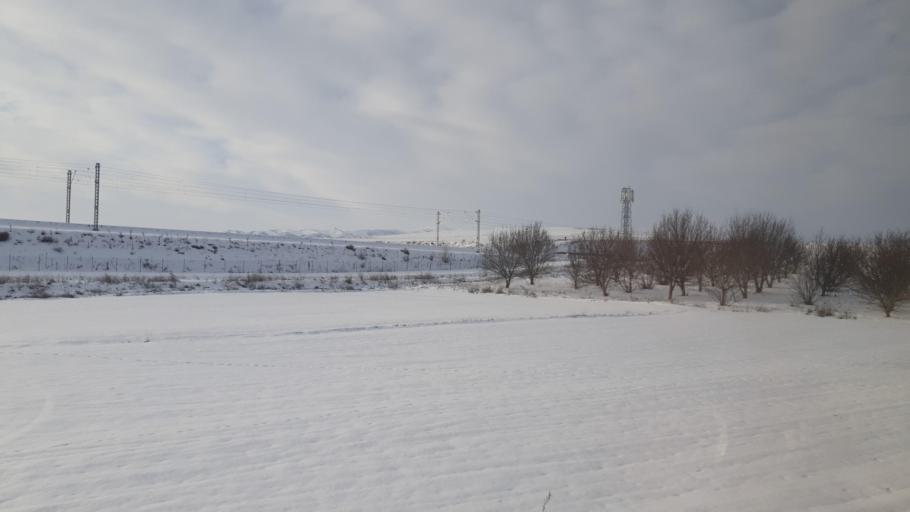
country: TR
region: Kirikkale
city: Baliseyh
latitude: 39.9323
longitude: 33.7989
